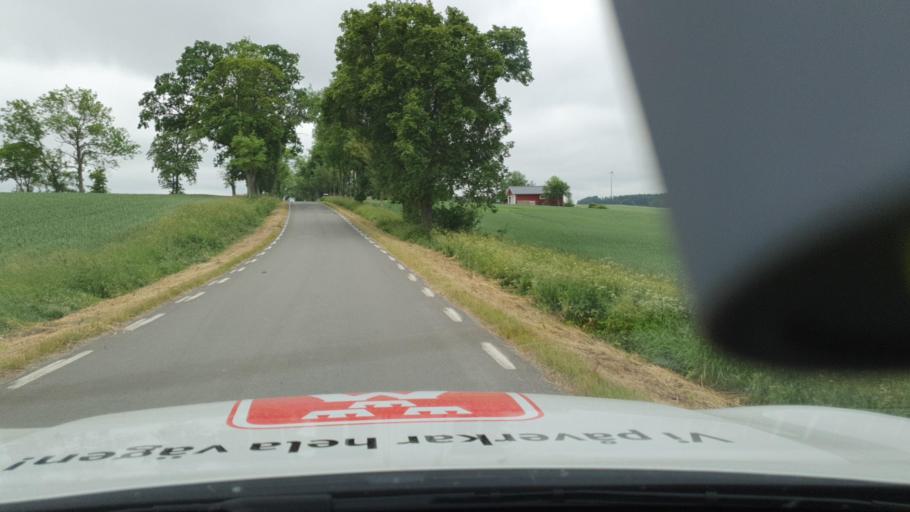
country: SE
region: Vaestra Goetaland
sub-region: Tibro Kommun
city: Tibro
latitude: 58.3705
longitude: 14.0994
